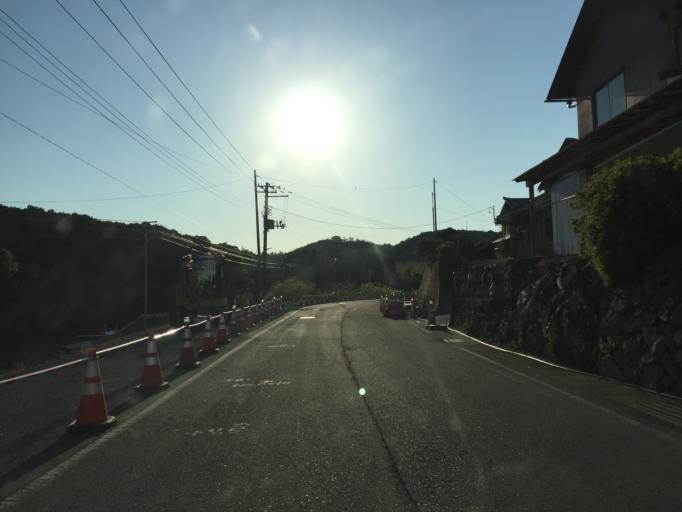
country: JP
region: Fukushima
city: Ishikawa
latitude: 37.0459
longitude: 140.4287
